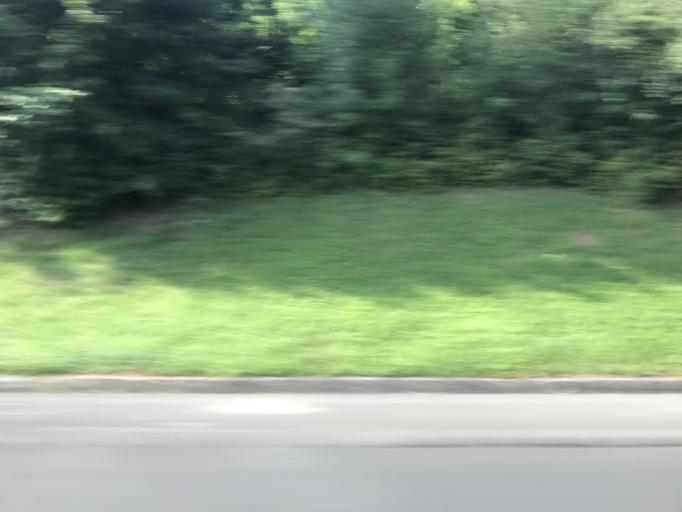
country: ES
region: Basque Country
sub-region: Provincia de Guipuzcoa
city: Beasain
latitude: 43.0461
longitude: -2.2087
